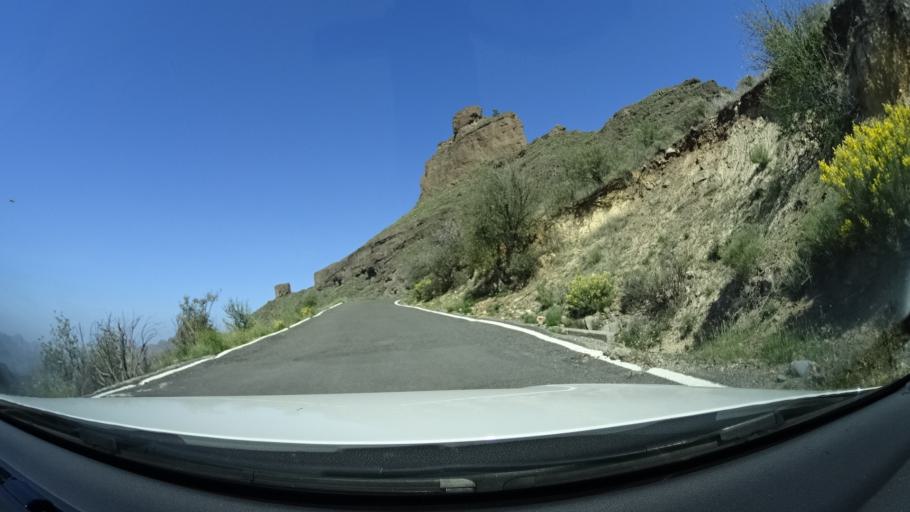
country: ES
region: Canary Islands
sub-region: Provincia de Las Palmas
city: Tejeda
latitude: 27.9878
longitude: -15.6397
